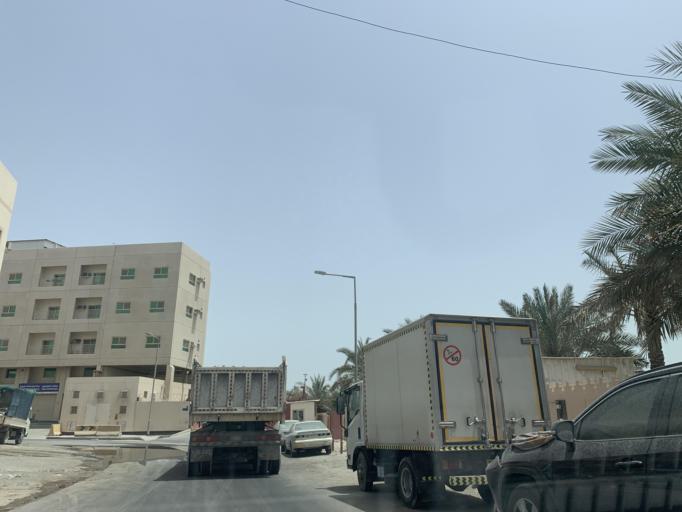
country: BH
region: Northern
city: Ar Rifa'
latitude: 26.1346
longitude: 50.5867
